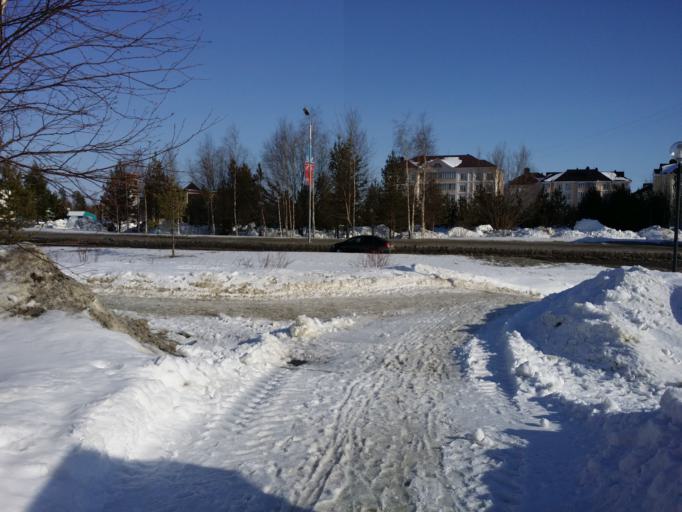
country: RU
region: Khanty-Mansiyskiy Avtonomnyy Okrug
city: Langepas
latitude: 61.2458
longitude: 75.1880
